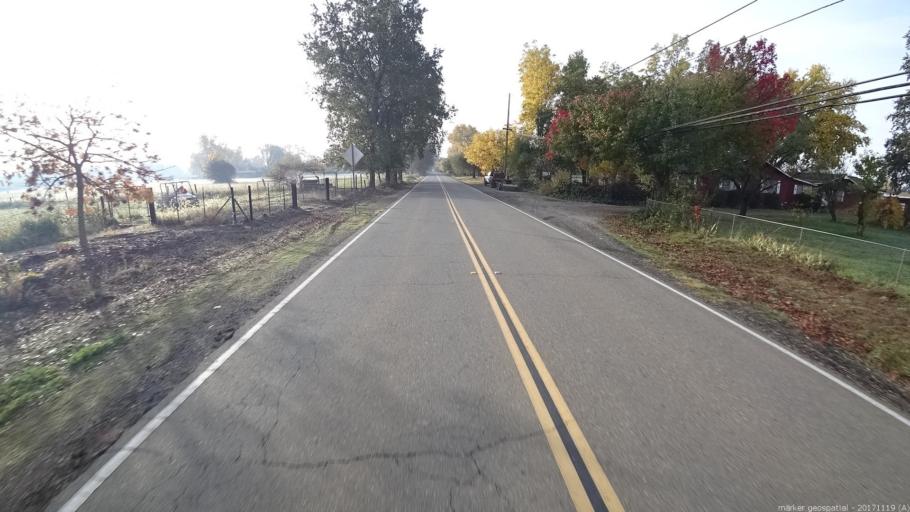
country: US
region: California
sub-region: Shasta County
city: Anderson
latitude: 40.5042
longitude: -122.3241
